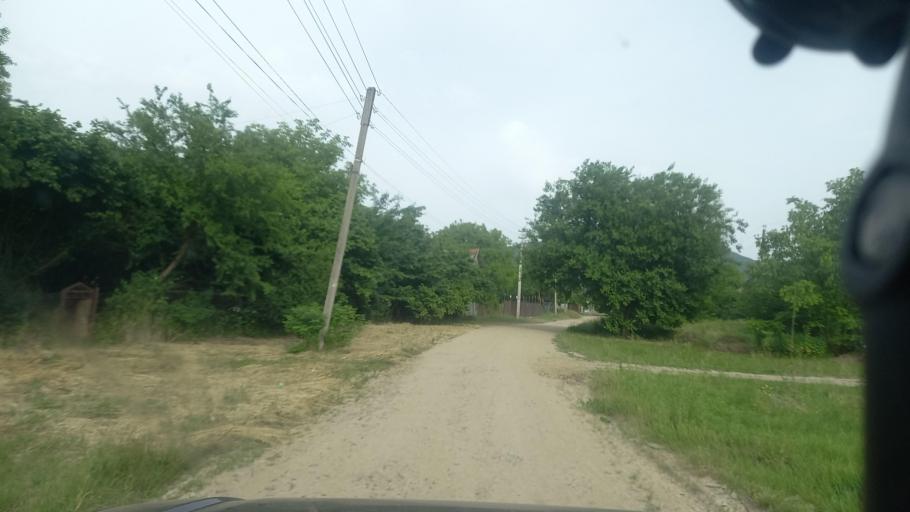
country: RU
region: Krasnodarskiy
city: Goryachiy Klyuch
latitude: 44.6046
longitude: 39.0301
